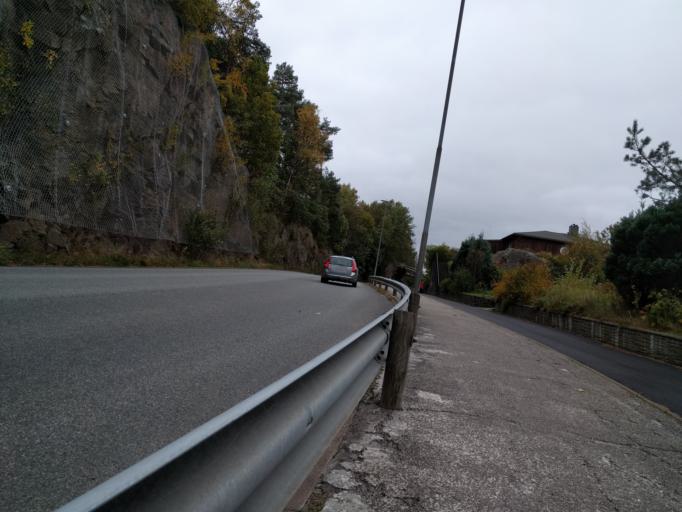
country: NO
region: Vest-Agder
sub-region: Kristiansand
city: Kristiansand
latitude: 58.1455
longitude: 7.9702
